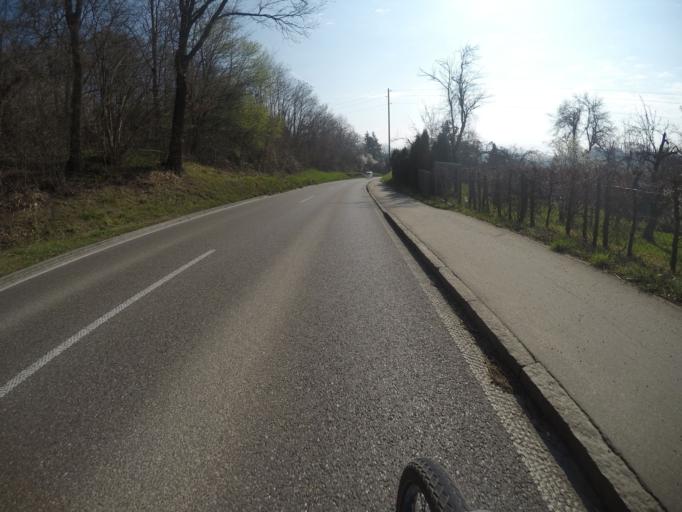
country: DE
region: Baden-Wuerttemberg
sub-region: Regierungsbezirk Stuttgart
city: Nurtingen
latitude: 48.6414
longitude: 9.3152
